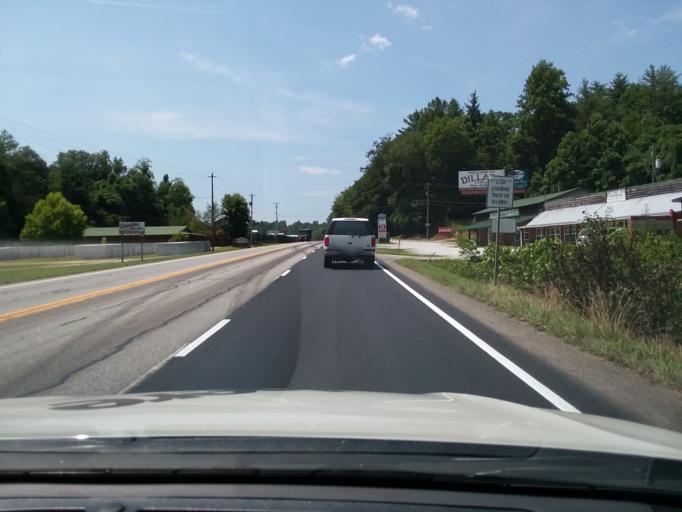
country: US
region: Georgia
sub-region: Rabun County
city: Mountain City
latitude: 34.9891
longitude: -83.3837
